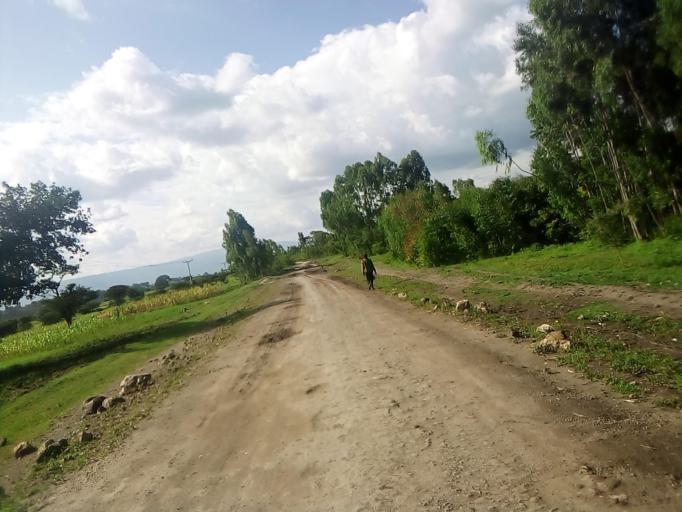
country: ET
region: Southern Nations, Nationalities, and People's Region
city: K'olito
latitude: 7.6505
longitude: 38.0509
